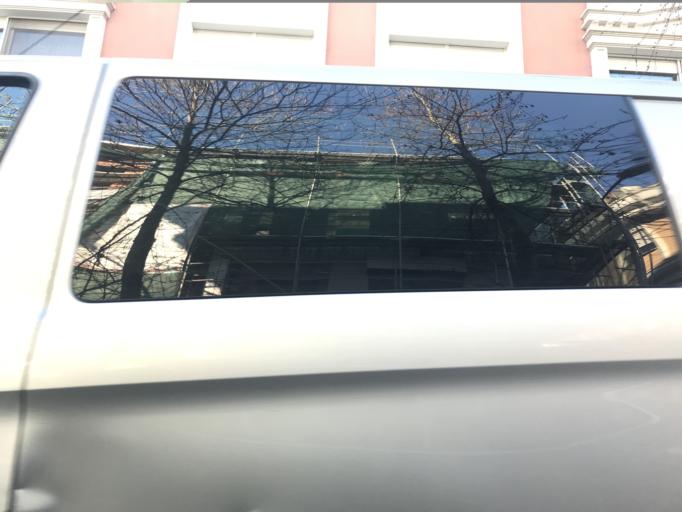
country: TR
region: Istanbul
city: Bahcelievler
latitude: 40.9620
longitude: 28.8337
